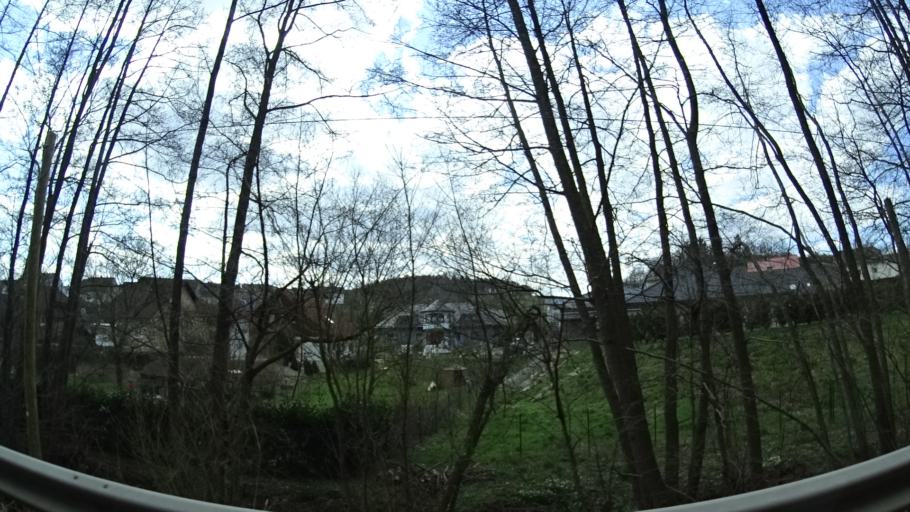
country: DE
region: Rheinland-Pfalz
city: Niederworresbach
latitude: 49.7718
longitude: 7.3309
